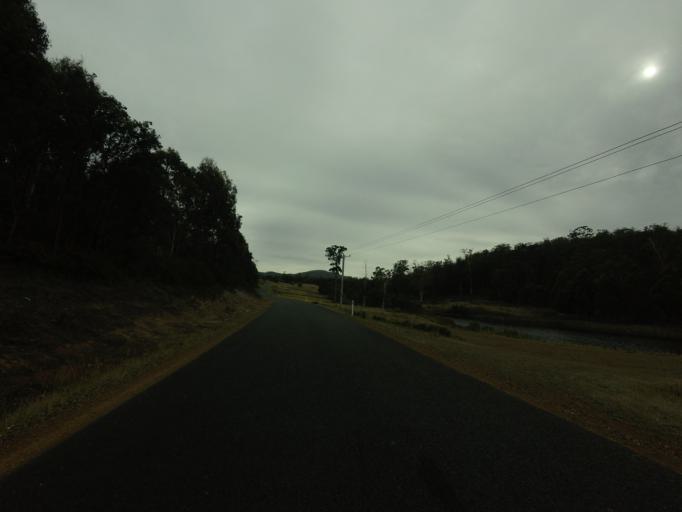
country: AU
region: Tasmania
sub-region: Sorell
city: Sorell
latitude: -42.5495
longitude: 147.5674
